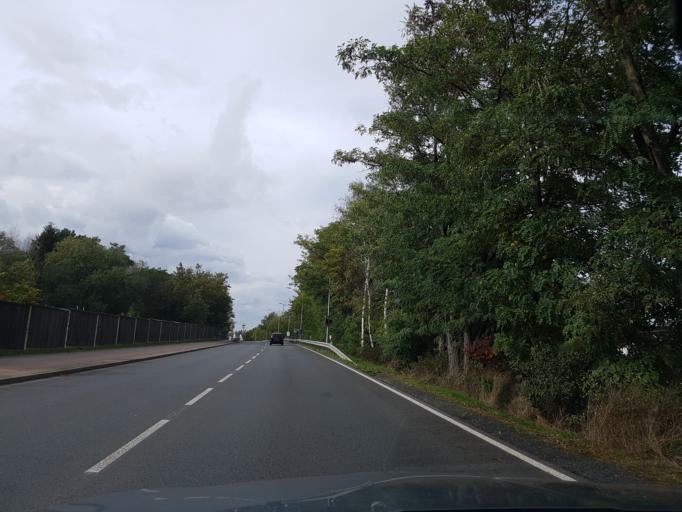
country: DE
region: Saxony
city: Riesa
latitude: 51.2931
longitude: 13.2920
